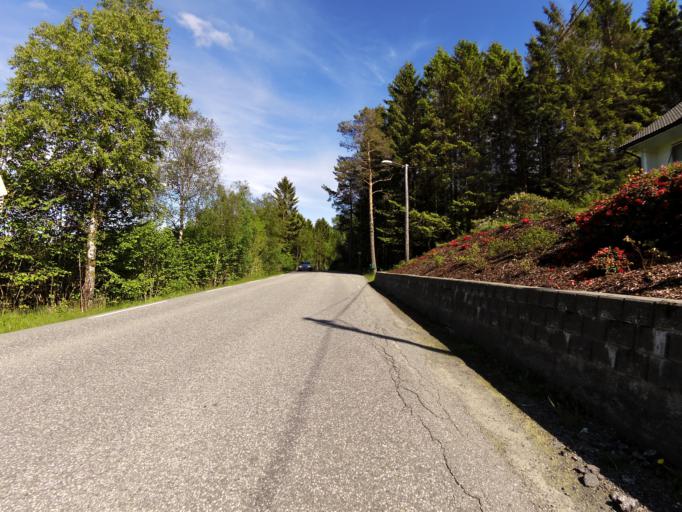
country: NO
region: Hordaland
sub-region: Stord
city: Leirvik
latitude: 59.7879
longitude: 5.4747
